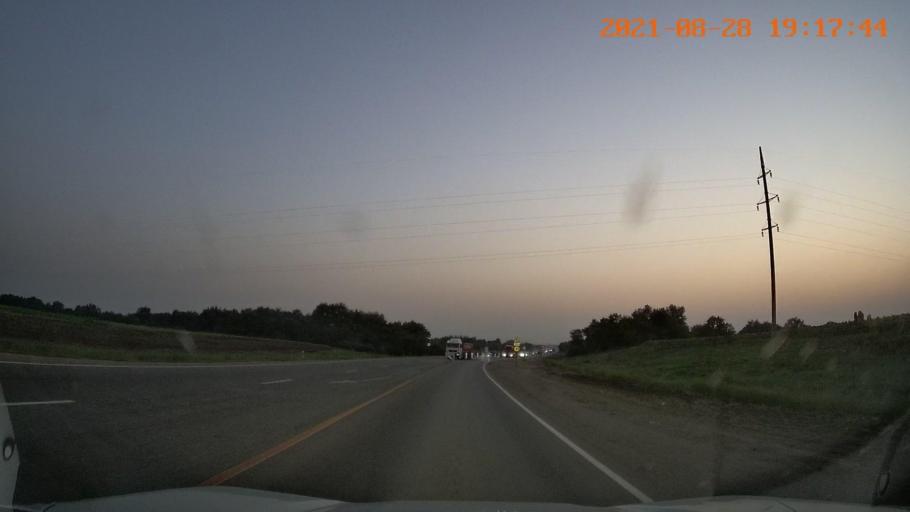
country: RU
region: Krasnodarskiy
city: Ryazanskaya
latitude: 44.8964
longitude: 39.5360
